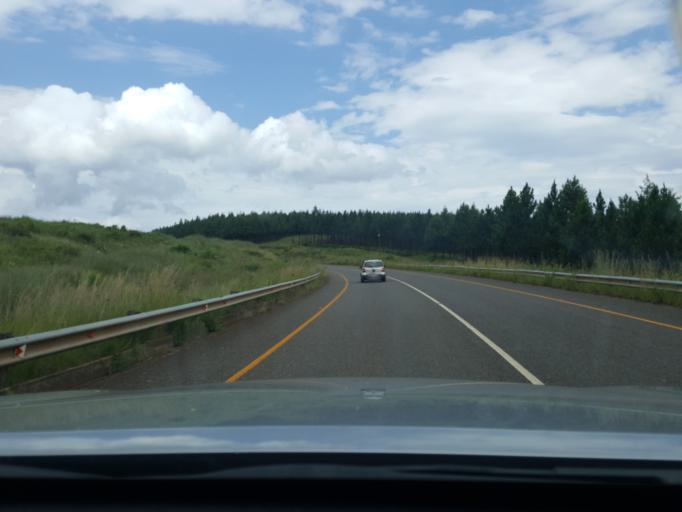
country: ZA
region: Mpumalanga
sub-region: Ehlanzeni District
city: Graksop
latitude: -25.1297
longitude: 30.8106
